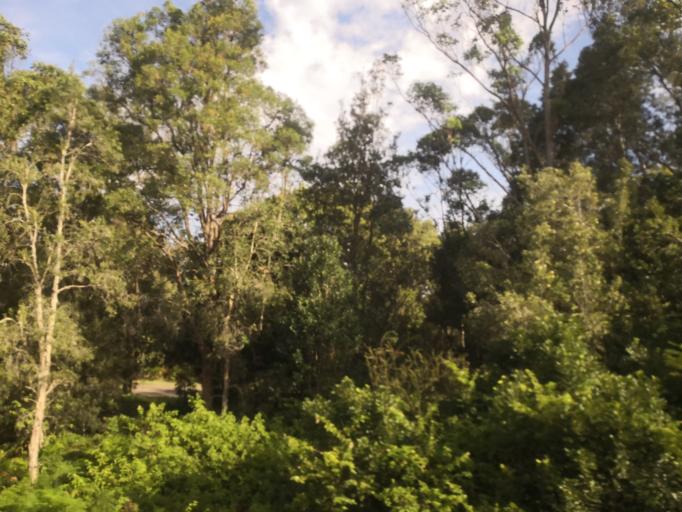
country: AU
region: New South Wales
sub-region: Gosford Shire
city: Blackwall
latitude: -33.4971
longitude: 151.3062
